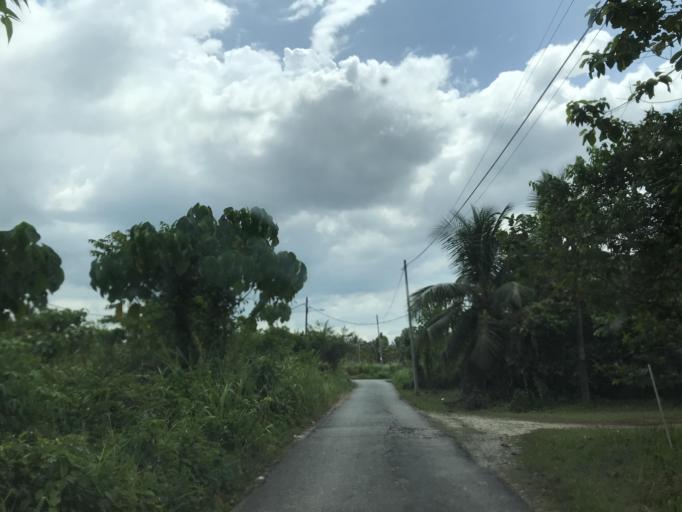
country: MY
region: Kelantan
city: Kota Bharu
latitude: 6.1122
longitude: 102.1844
